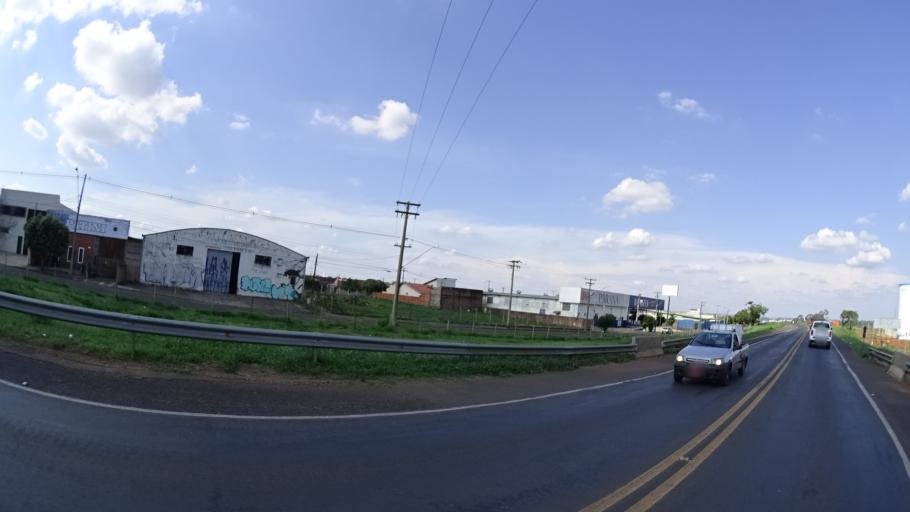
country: BR
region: Sao Paulo
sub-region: Sao Jose Do Rio Preto
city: Sao Jose do Rio Preto
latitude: -20.8506
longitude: -49.3815
